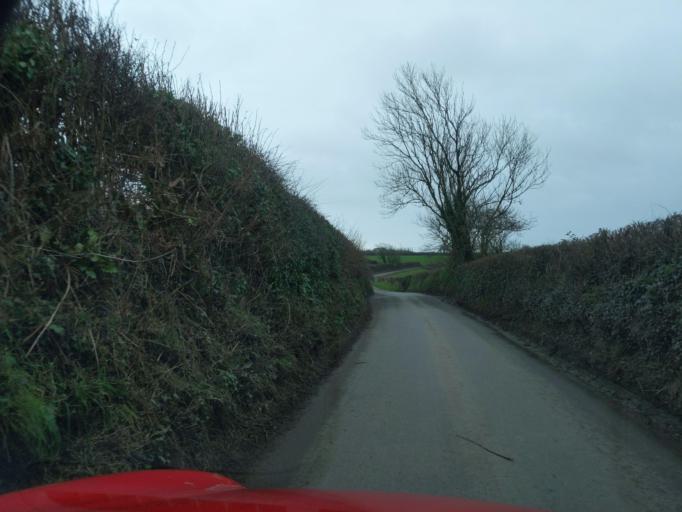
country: GB
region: England
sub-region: Devon
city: Modbury
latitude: 50.3362
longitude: -3.8687
